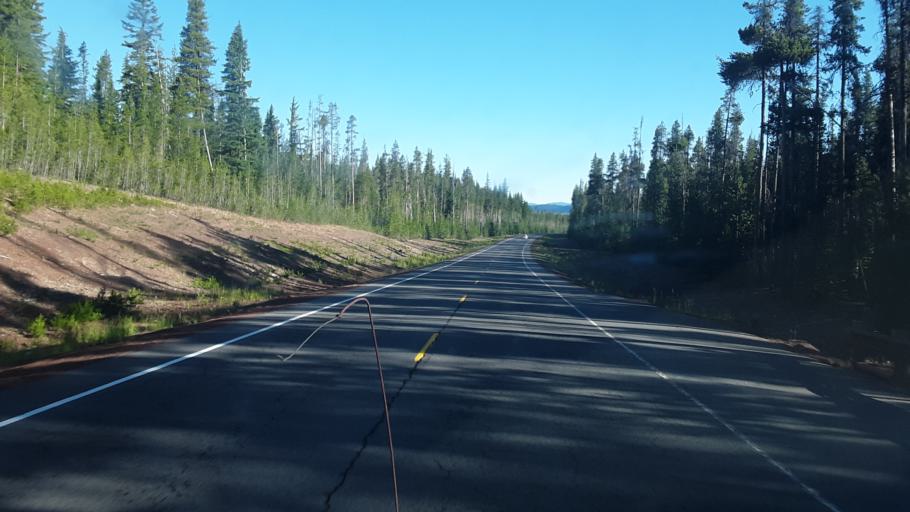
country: US
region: Oregon
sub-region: Lane County
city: Oakridge
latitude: 43.1114
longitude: -122.1317
